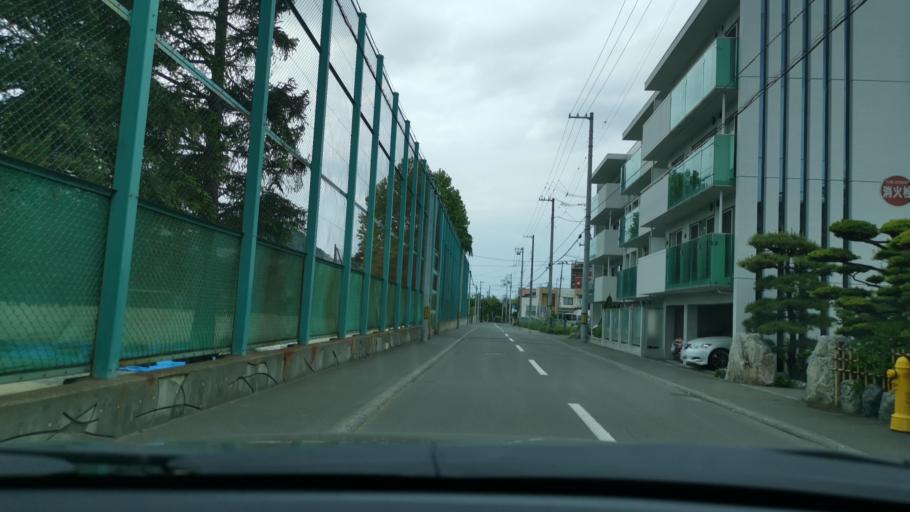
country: JP
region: Hokkaido
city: Sapporo
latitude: 43.0377
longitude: 141.3344
